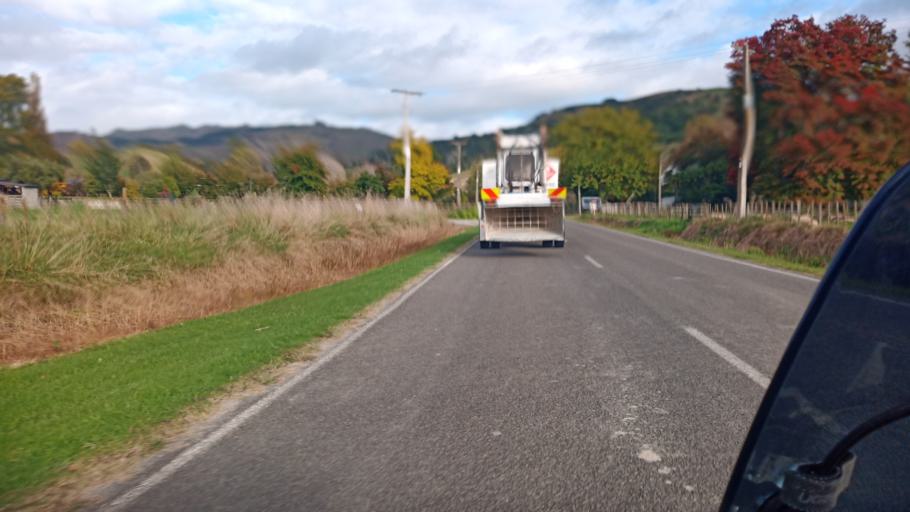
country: NZ
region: Gisborne
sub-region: Gisborne District
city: Gisborne
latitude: -38.5857
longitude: 177.7923
